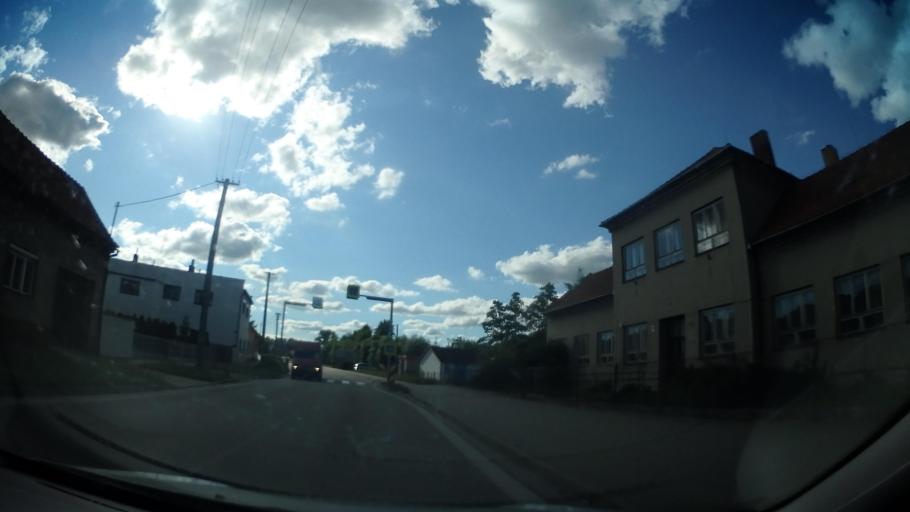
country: CZ
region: South Moravian
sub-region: Okres Blansko
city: Rajec-Jestrebi
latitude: 49.4107
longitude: 16.6185
